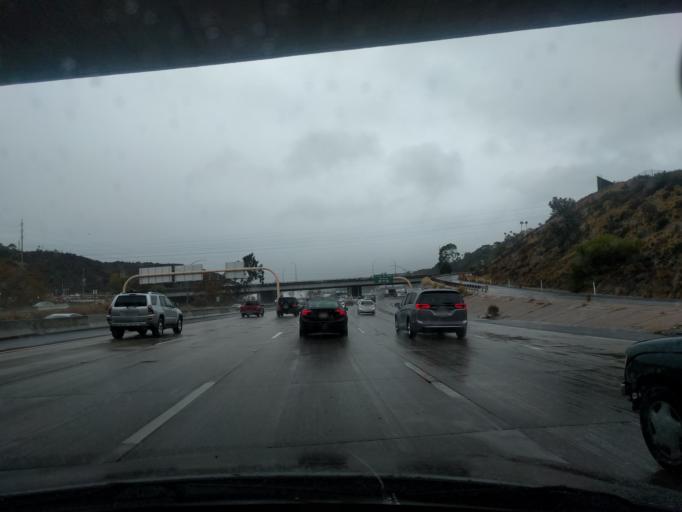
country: US
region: California
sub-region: San Diego County
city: San Diego
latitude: 32.7861
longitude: -117.1142
